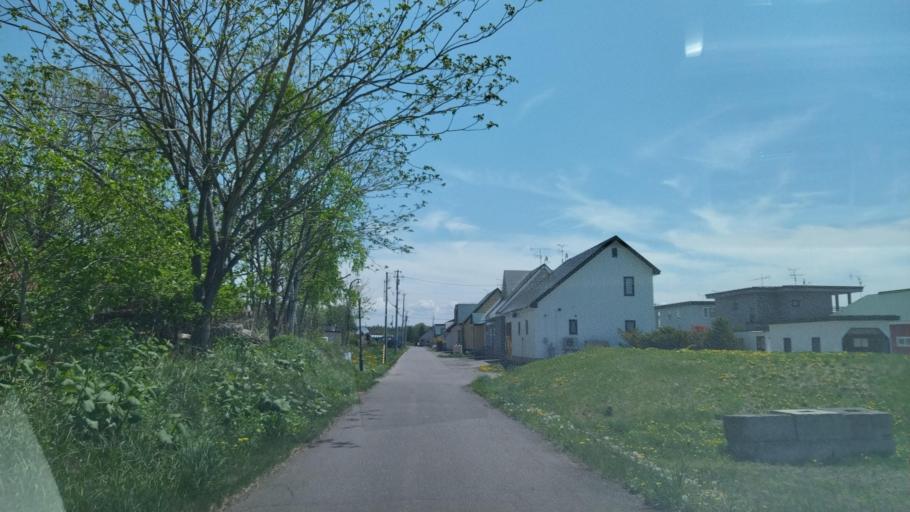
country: JP
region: Hokkaido
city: Otofuke
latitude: 43.2274
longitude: 143.2868
